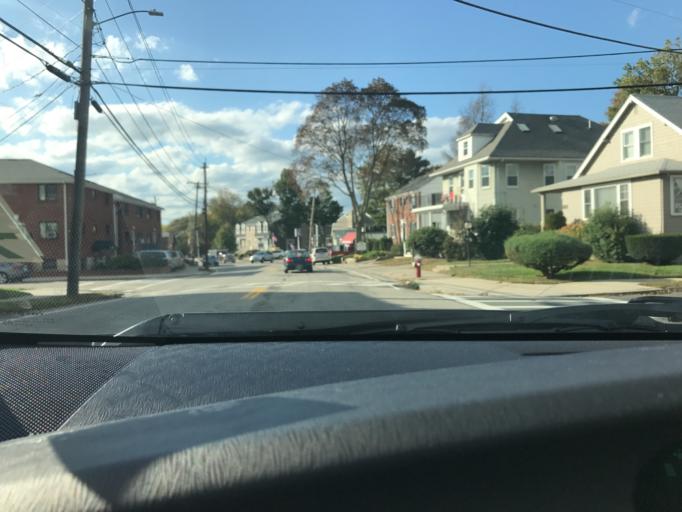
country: US
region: Massachusetts
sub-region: Middlesex County
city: Watertown
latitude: 42.3821
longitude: -71.1962
